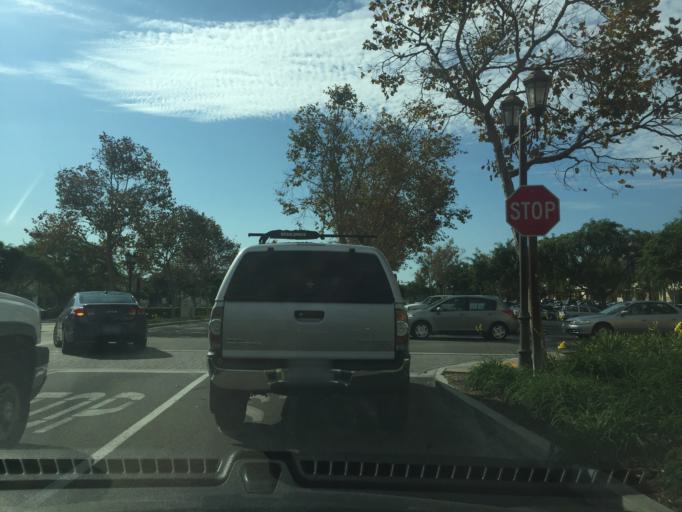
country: US
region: California
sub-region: Santa Barbara County
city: Isla Vista
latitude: 34.4294
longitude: -119.8736
